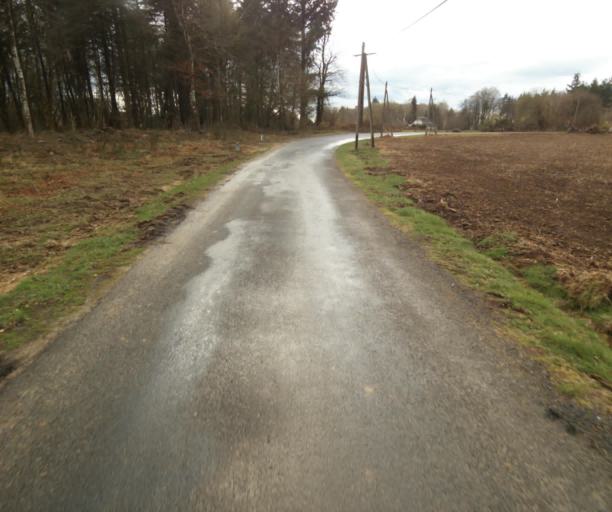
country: FR
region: Limousin
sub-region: Departement de la Correze
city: Saint-Privat
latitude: 45.2246
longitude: 2.0095
